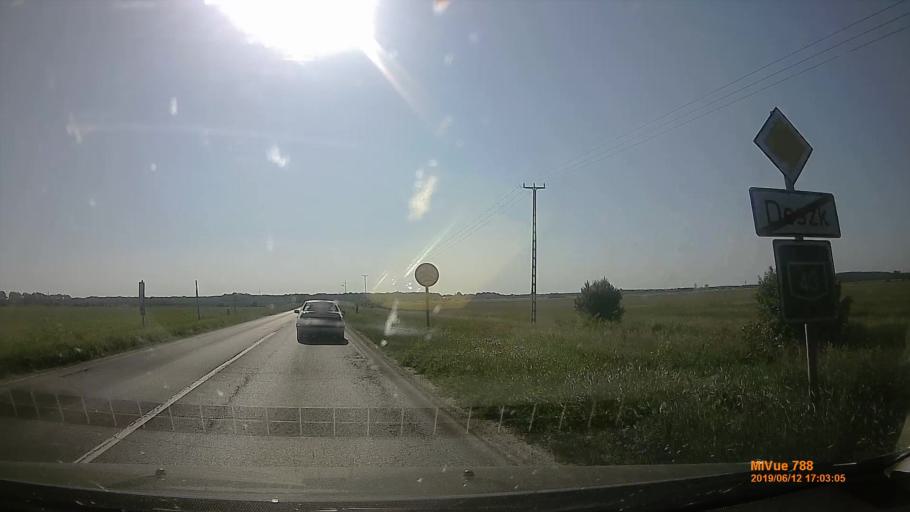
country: HU
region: Csongrad
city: Deszk
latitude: 46.2148
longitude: 20.2252
